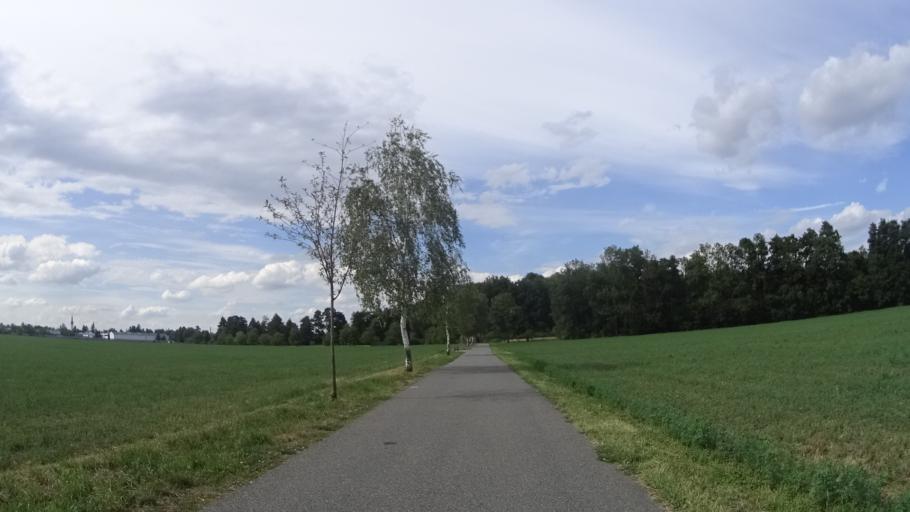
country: CZ
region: Olomoucky
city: Litovel
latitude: 49.6958
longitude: 17.0934
